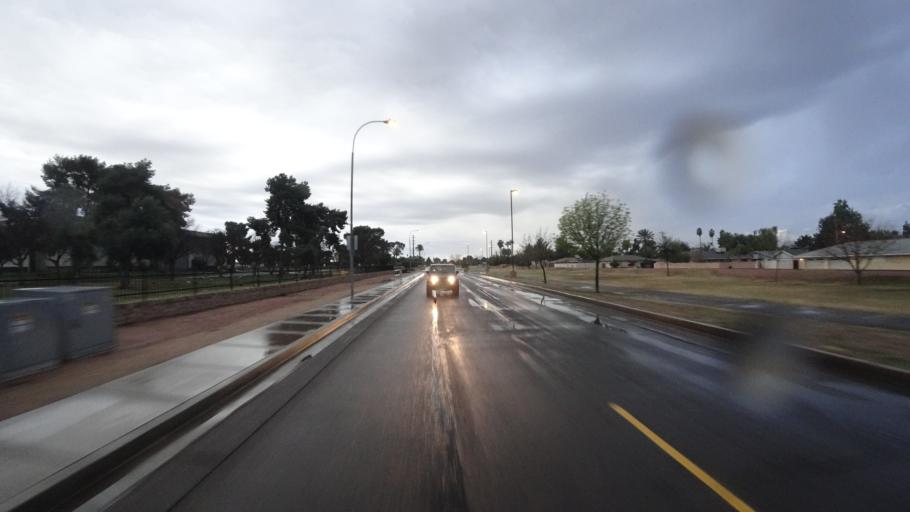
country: US
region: Arizona
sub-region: Maricopa County
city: Paradise Valley
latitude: 33.4746
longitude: -111.9781
